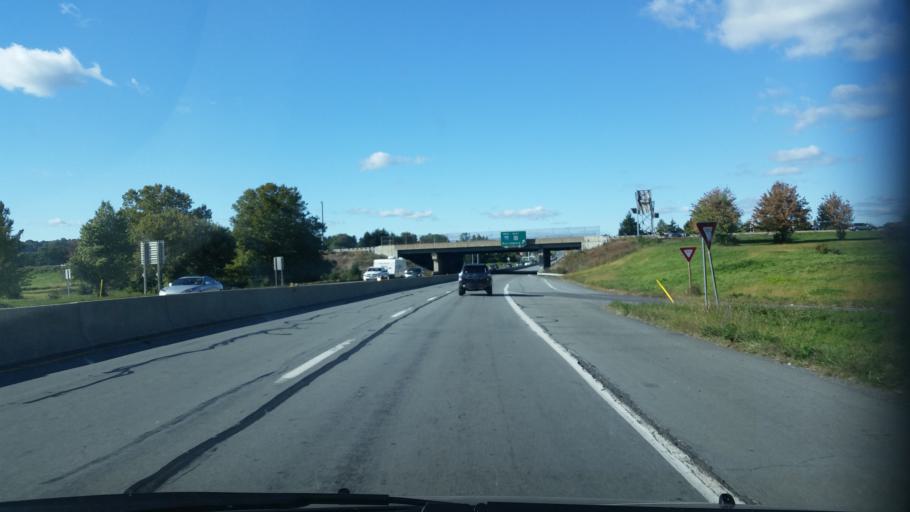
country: US
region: Pennsylvania
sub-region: Lehigh County
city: Trexlertown
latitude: 40.5785
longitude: -75.6234
